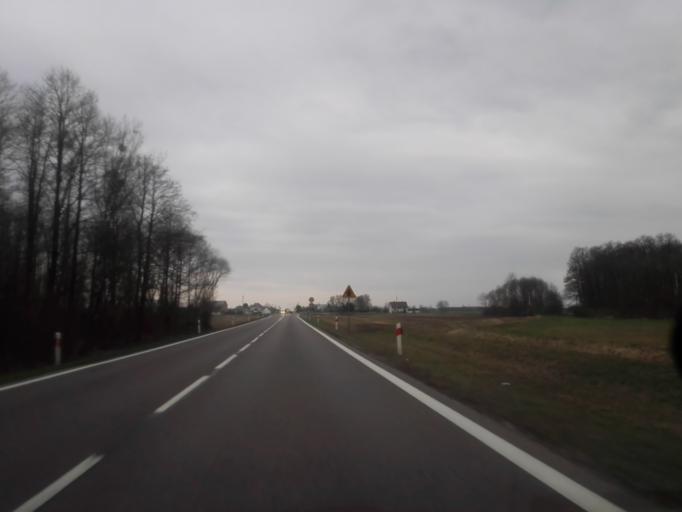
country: PL
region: Podlasie
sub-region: Powiat grajewski
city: Rajgrod
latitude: 53.6875
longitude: 22.6270
